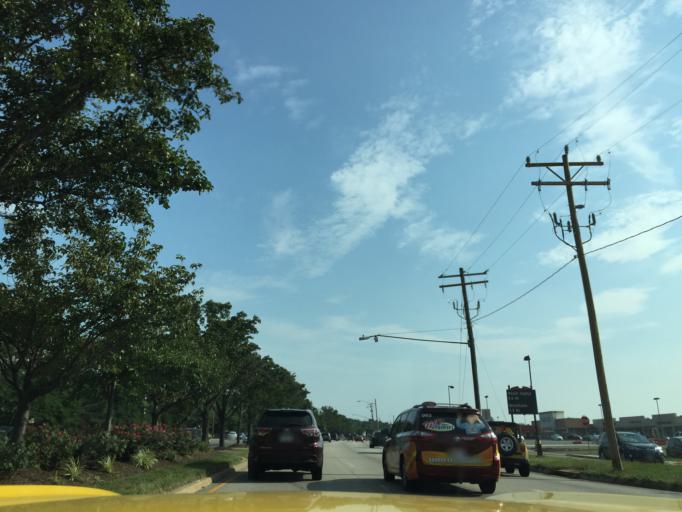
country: US
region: Virginia
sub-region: Fairfax County
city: Hybla Valley
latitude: 38.7469
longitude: -77.0833
